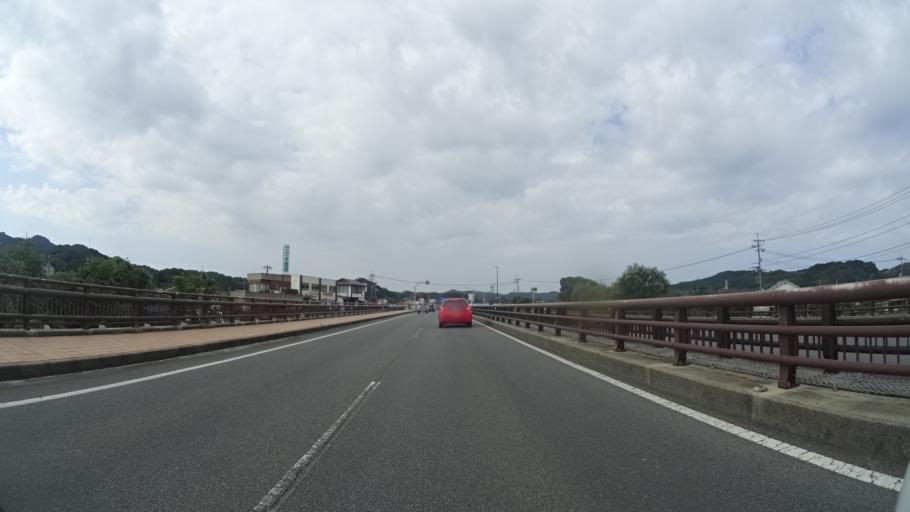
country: JP
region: Shimane
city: Odacho-oda
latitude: 35.2006
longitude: 132.4931
